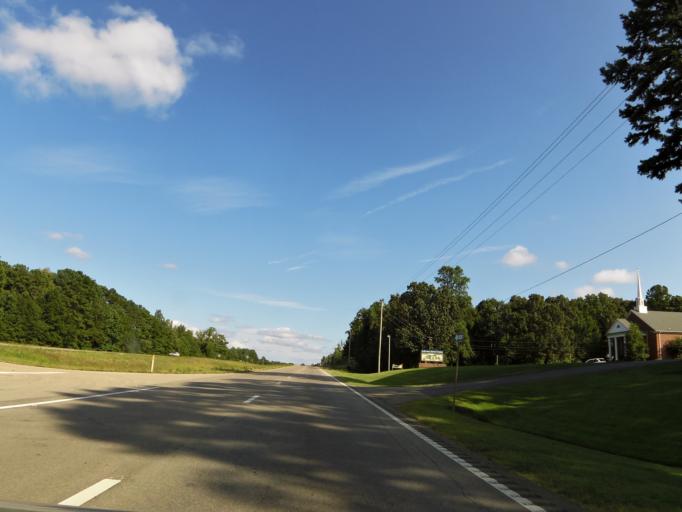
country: US
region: Mississippi
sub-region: Alcorn County
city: Farmington
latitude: 34.8681
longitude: -88.4230
